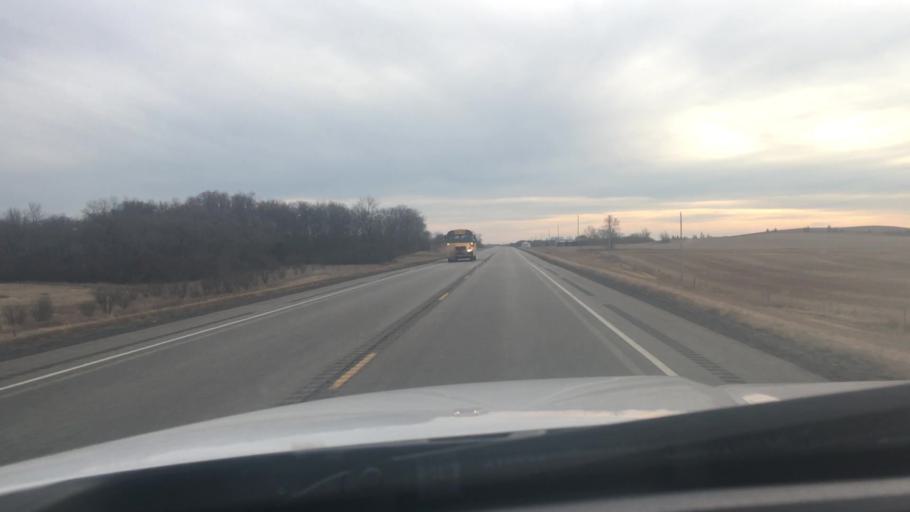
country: US
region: Minnesota
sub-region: Otter Tail County
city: Perham
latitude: 46.3318
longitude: -95.7185
